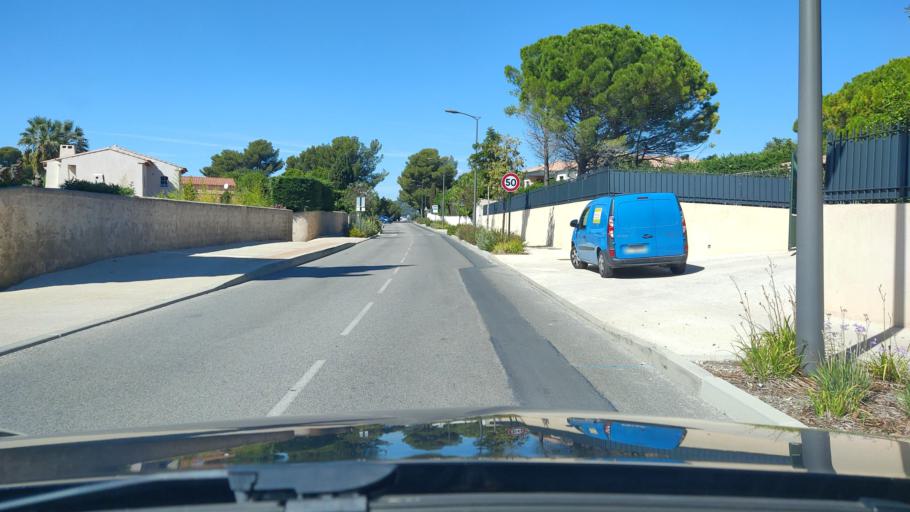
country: FR
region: Provence-Alpes-Cote d'Azur
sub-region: Departement du Var
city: Sanary-sur-Mer
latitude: 43.1330
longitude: 5.7910
